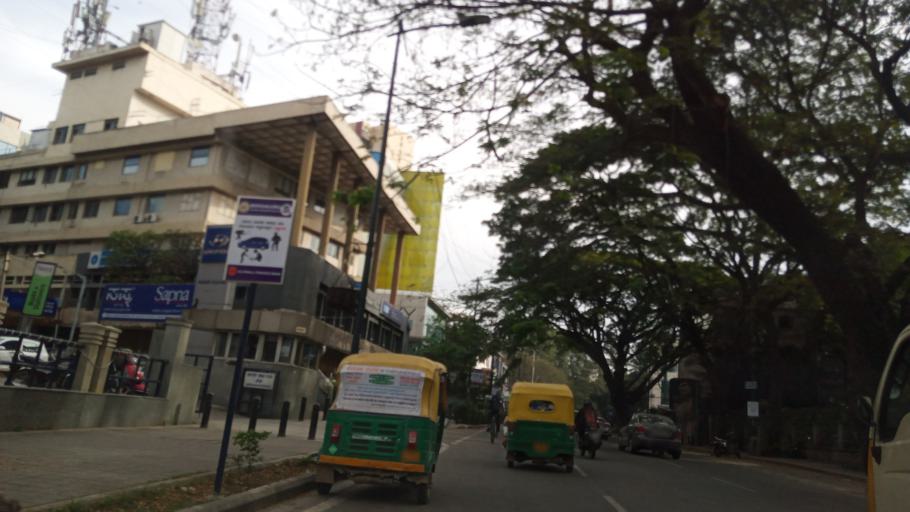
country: IN
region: Karnataka
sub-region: Bangalore Urban
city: Bangalore
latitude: 12.9726
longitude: 77.6082
